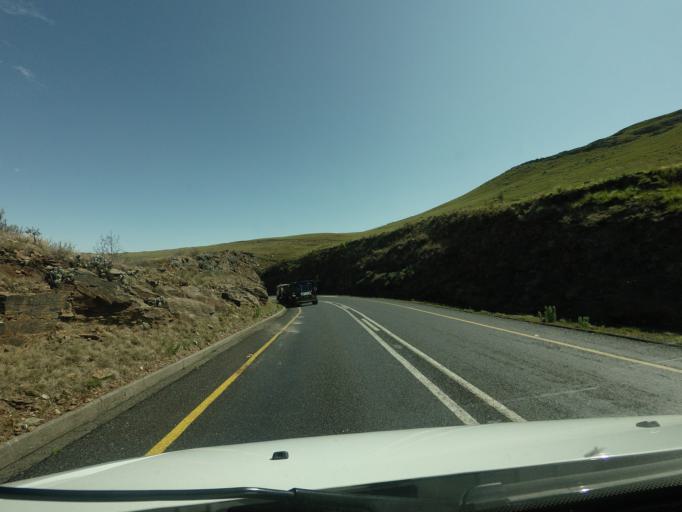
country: ZA
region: Mpumalanga
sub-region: Ehlanzeni District
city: Lydenburg
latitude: -25.1553
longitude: 30.6248
